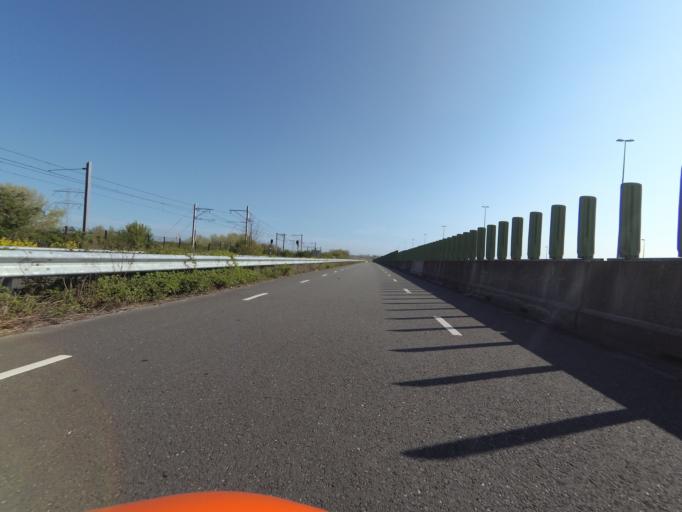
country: NL
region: North Holland
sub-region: Gemeente Naarden
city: Naarden
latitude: 52.3278
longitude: 5.1430
